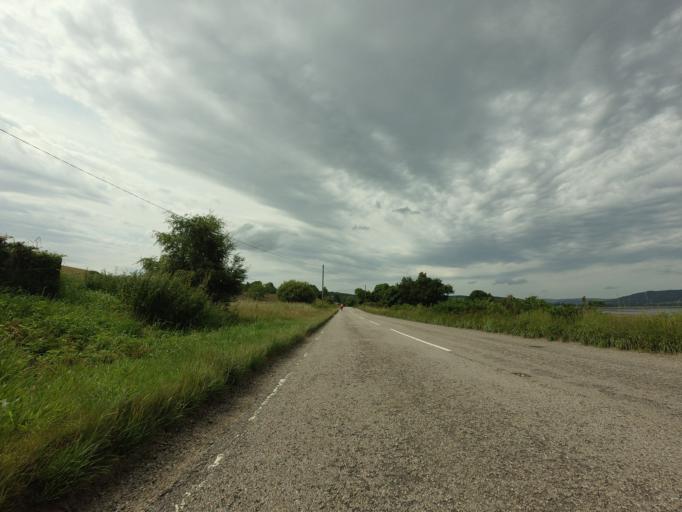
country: GB
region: Scotland
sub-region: Highland
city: Alness
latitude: 57.8707
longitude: -4.3463
